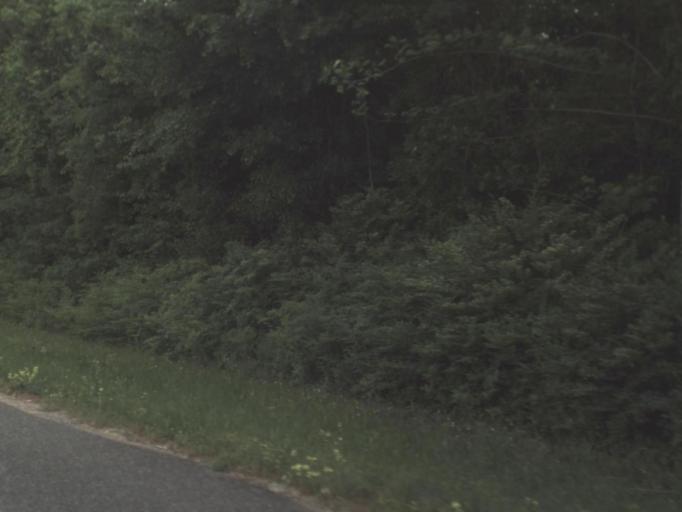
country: US
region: Florida
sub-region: Santa Rosa County
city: Point Baker
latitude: 30.7532
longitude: -87.0425
